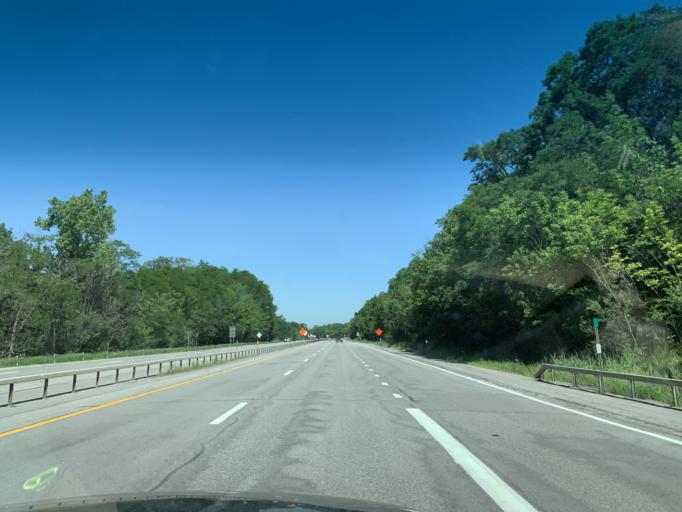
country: US
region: New York
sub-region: Oneida County
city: Chadwicks
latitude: 43.0095
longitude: -75.2543
